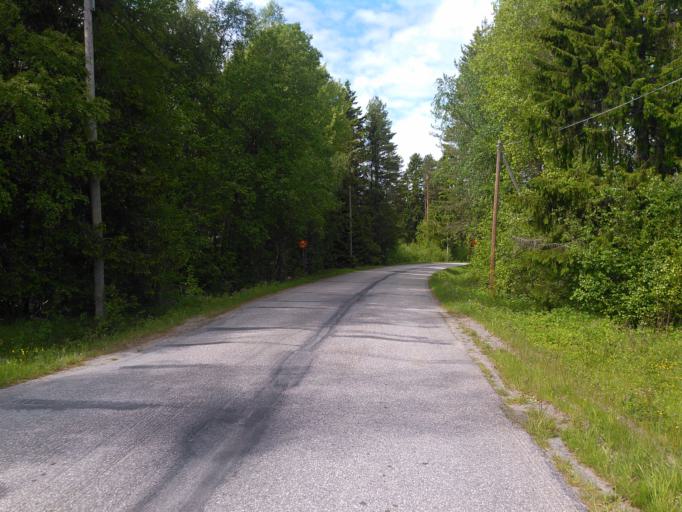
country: SE
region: Vaesterbotten
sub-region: Umea Kommun
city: Ersmark
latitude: 63.8772
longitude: 20.3219
